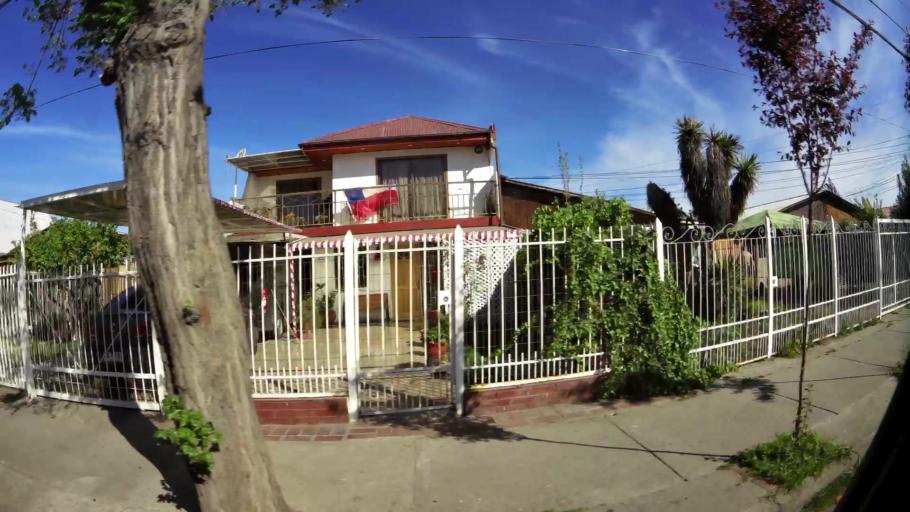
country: CL
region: Santiago Metropolitan
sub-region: Provincia de Santiago
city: Lo Prado
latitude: -33.4933
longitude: -70.7449
